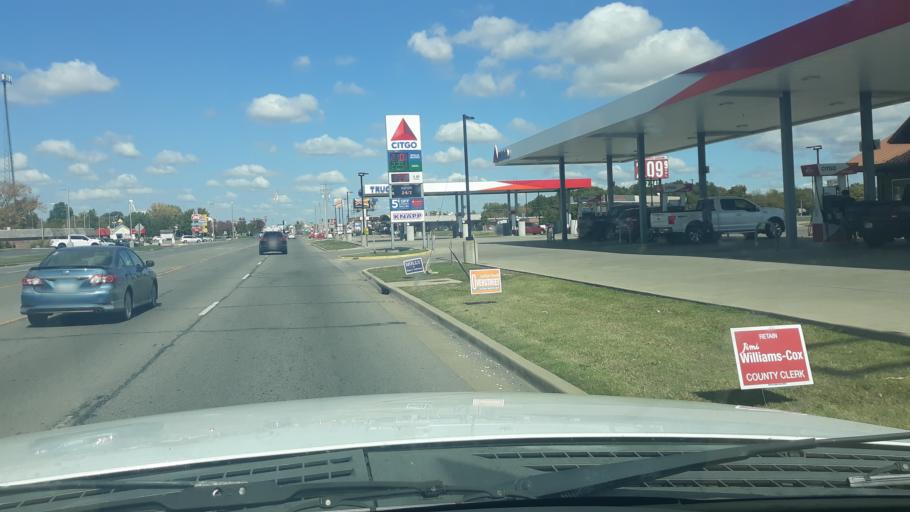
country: US
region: Illinois
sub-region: Saline County
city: Harrisburg
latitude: 37.7284
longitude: -88.5364
